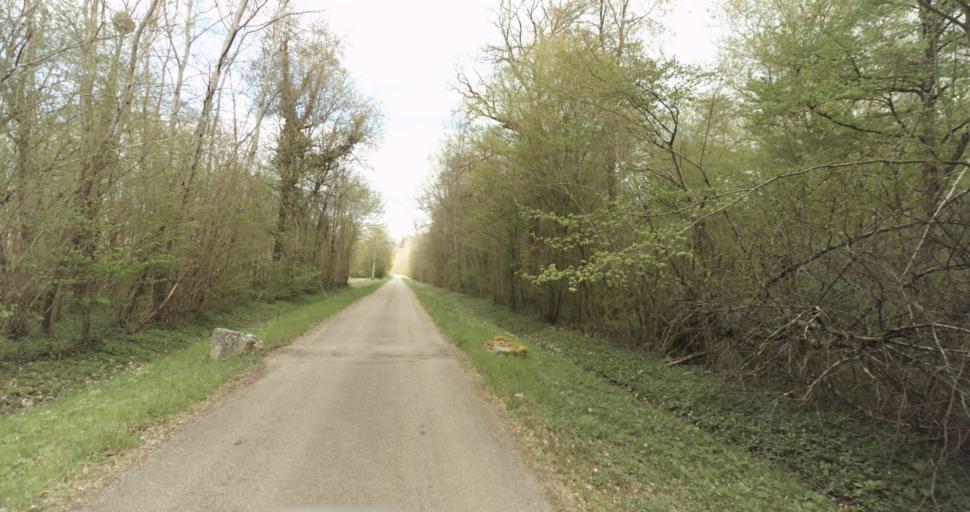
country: FR
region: Bourgogne
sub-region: Departement de la Cote-d'Or
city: Auxonne
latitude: 47.1860
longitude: 5.4497
